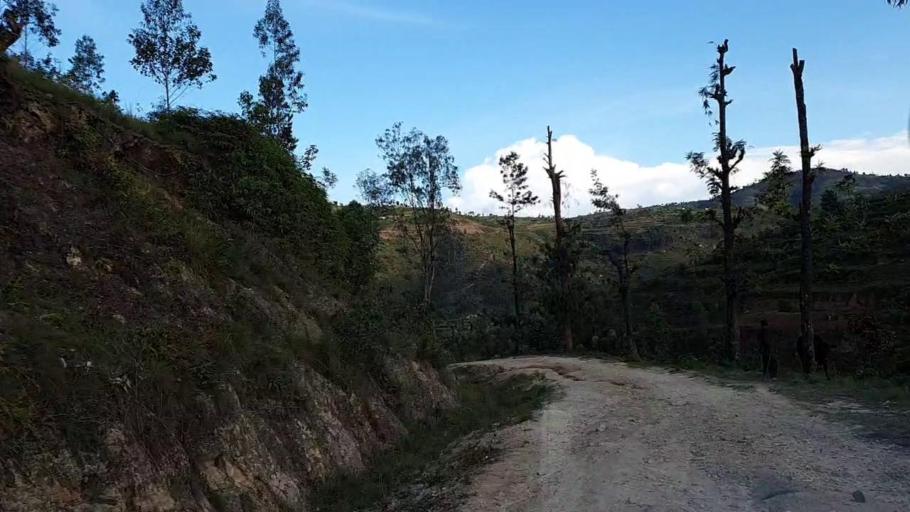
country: RW
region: Southern Province
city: Gikongoro
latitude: -2.4002
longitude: 29.5626
